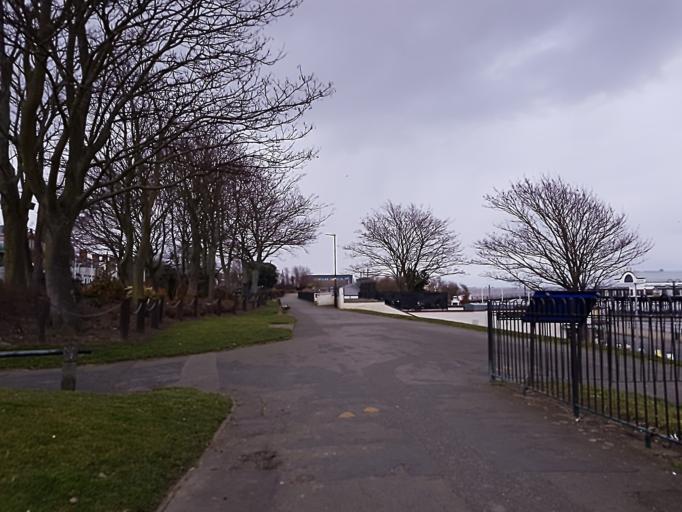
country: GB
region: England
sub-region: North East Lincolnshire
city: Cleethorpes
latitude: 53.5590
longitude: -0.0262
